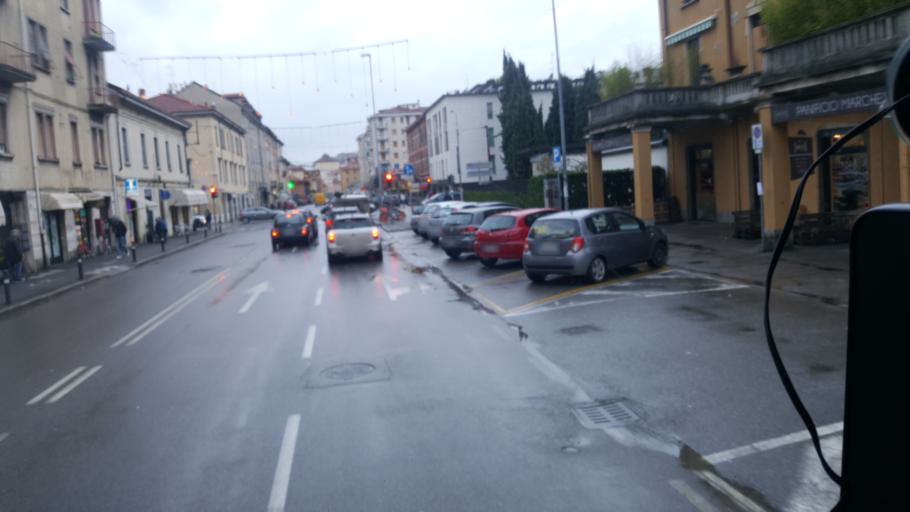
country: IT
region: Lombardy
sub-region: Provincia di Bergamo
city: Orio al Serio
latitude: 45.6944
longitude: 9.6894
